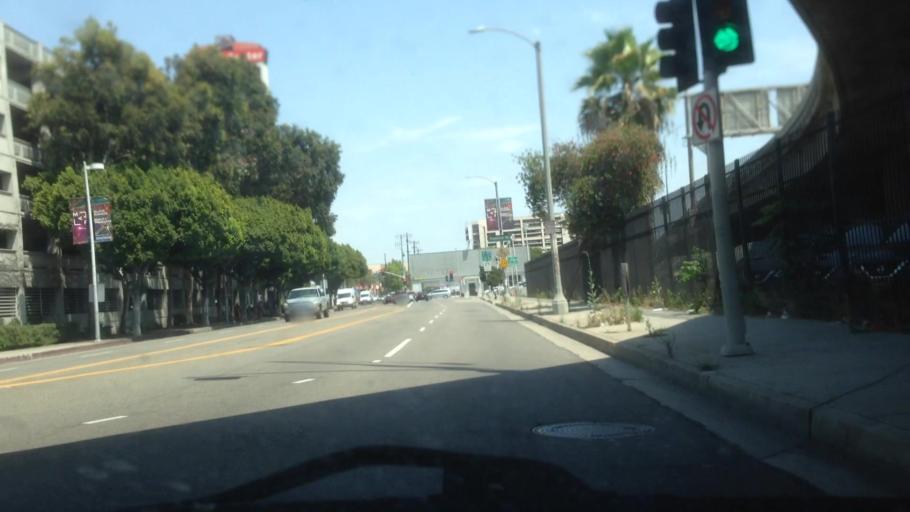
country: US
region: California
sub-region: Los Angeles County
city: Los Angeles
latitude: 34.0381
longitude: -118.2718
